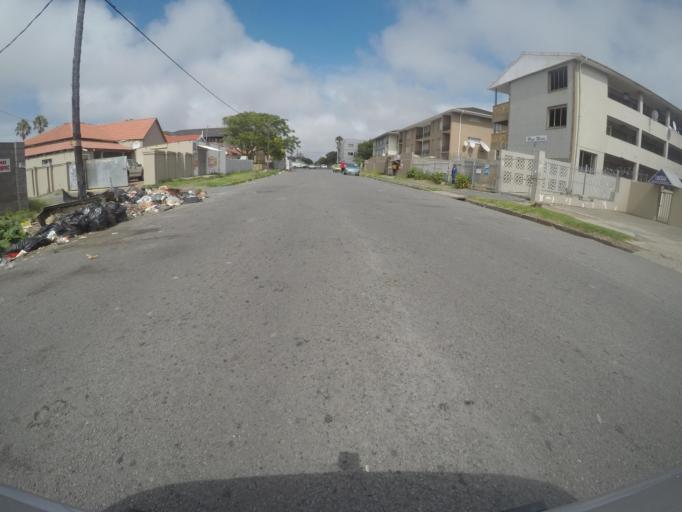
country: ZA
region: Eastern Cape
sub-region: Buffalo City Metropolitan Municipality
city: East London
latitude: -32.9994
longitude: 27.9059
